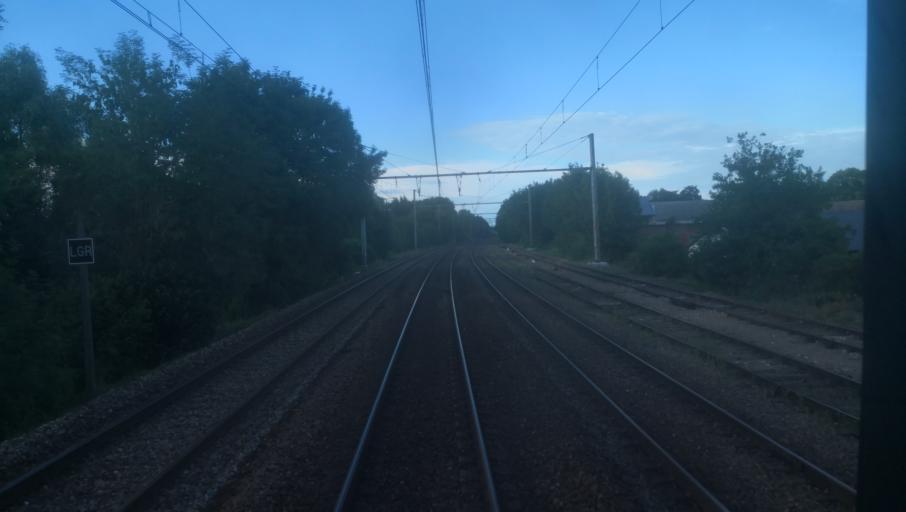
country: FR
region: Centre
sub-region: Departement de l'Indre
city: Issoudun
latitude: 46.9559
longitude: 1.9899
